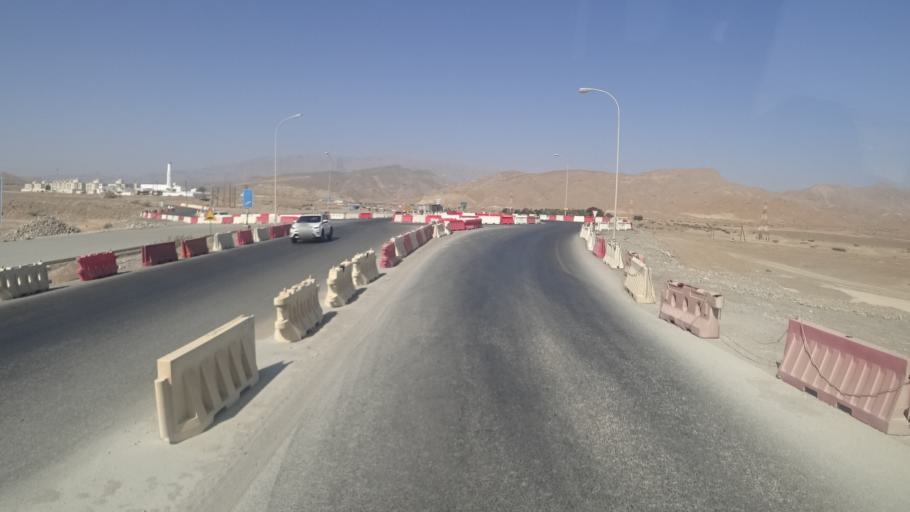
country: OM
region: Ash Sharqiyah
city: Sur
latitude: 22.5176
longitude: 59.4486
